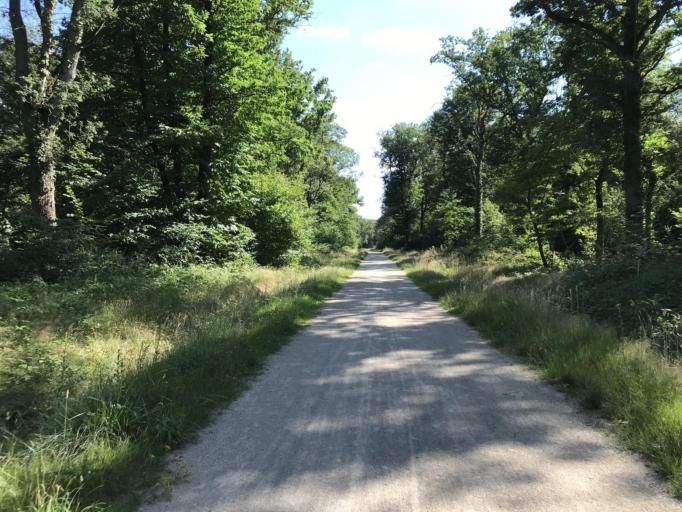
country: FR
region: Ile-de-France
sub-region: Departement de l'Essonne
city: Bondoufle
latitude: 48.6300
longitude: 2.3832
